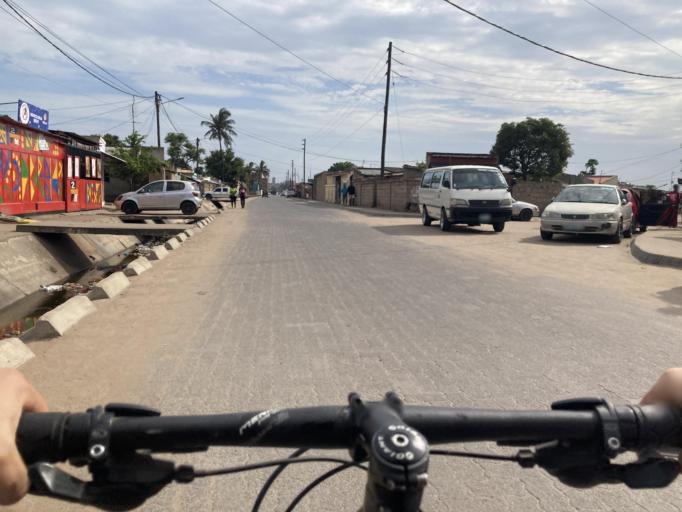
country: MZ
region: Maputo City
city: Maputo
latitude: -25.9419
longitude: 32.5838
